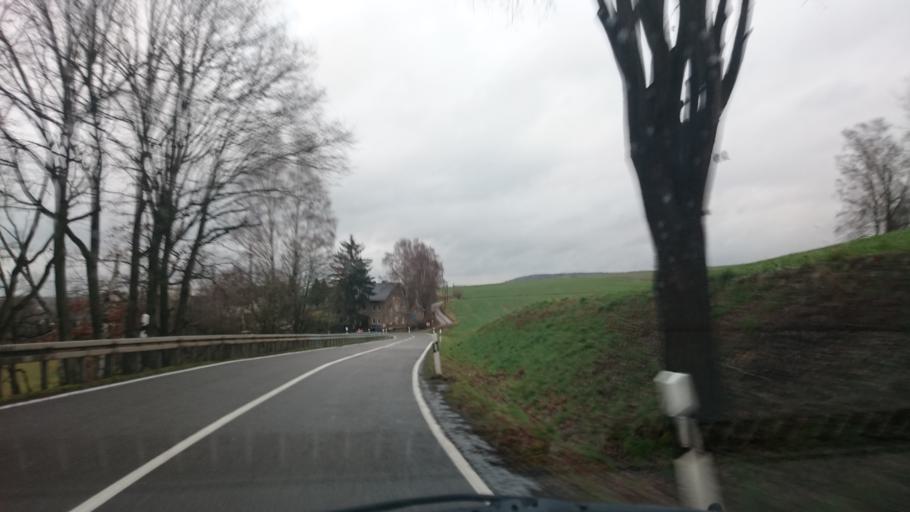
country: DE
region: Saxony
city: Sankt Egidien
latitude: 50.7776
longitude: 12.6183
